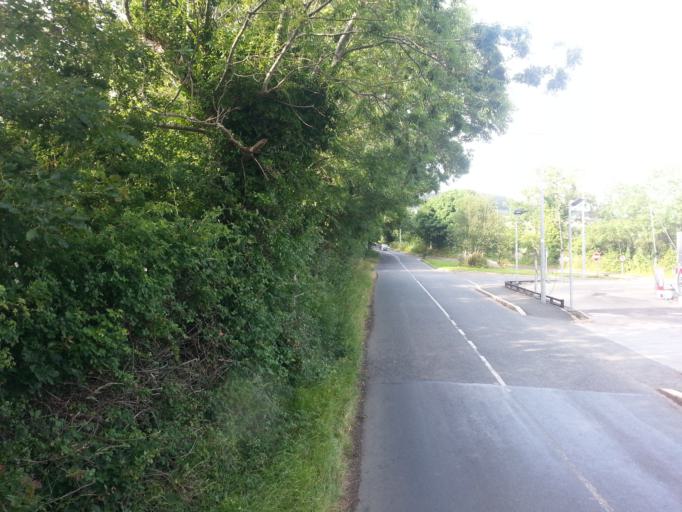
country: IE
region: Leinster
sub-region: Wicklow
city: Enniskerry
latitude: 53.2037
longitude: -6.1762
